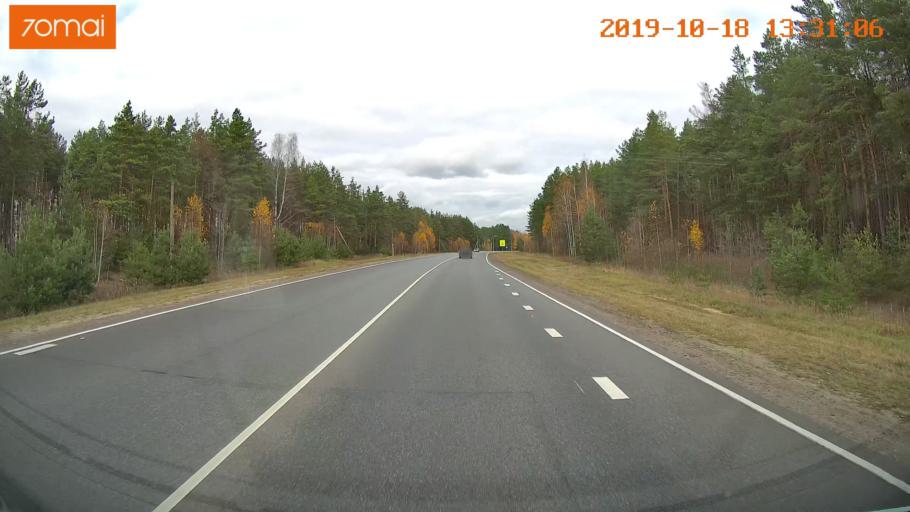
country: RU
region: Rjazan
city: Solotcha
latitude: 54.8182
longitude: 39.8952
